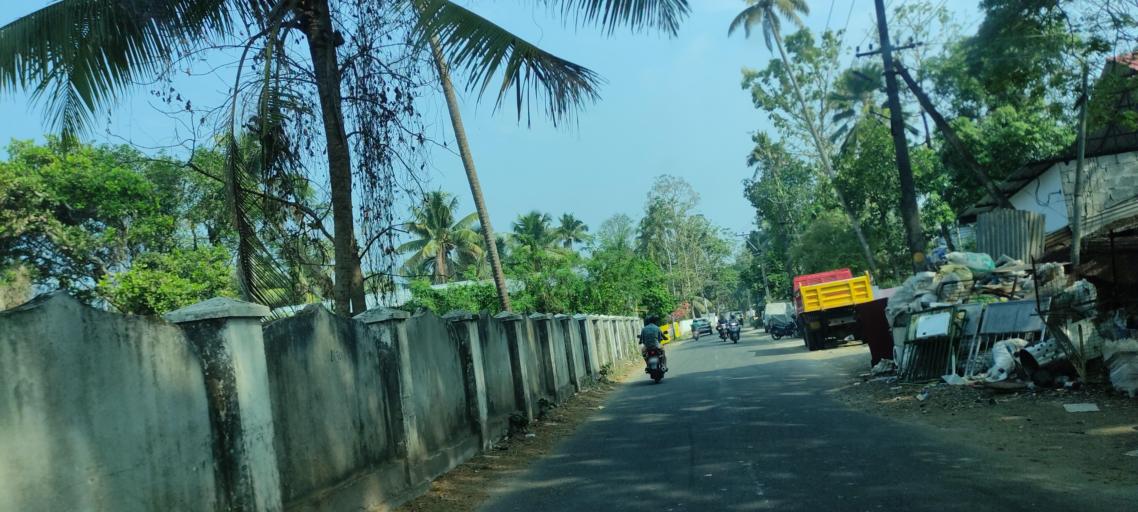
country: IN
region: Kerala
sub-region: Alappuzha
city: Kutiatodu
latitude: 9.7769
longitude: 76.3050
